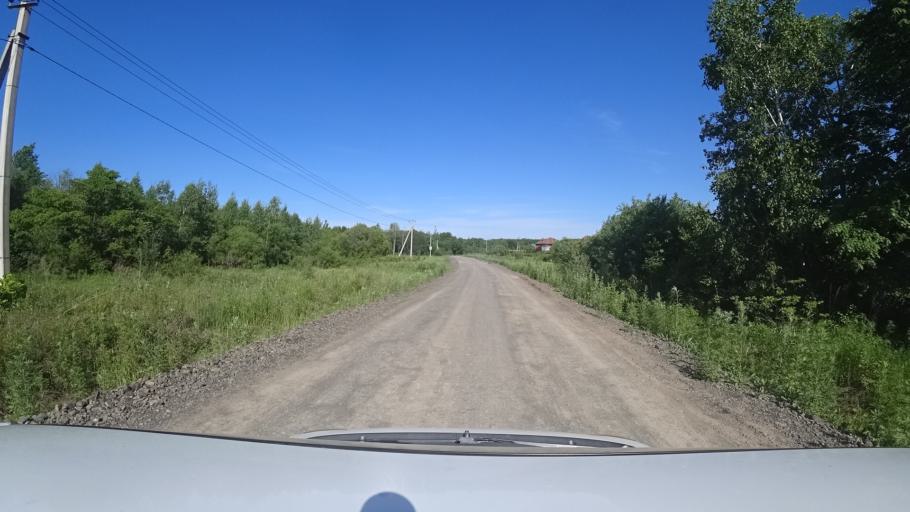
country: RU
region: Khabarovsk Krai
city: Topolevo
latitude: 48.5528
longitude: 135.1828
